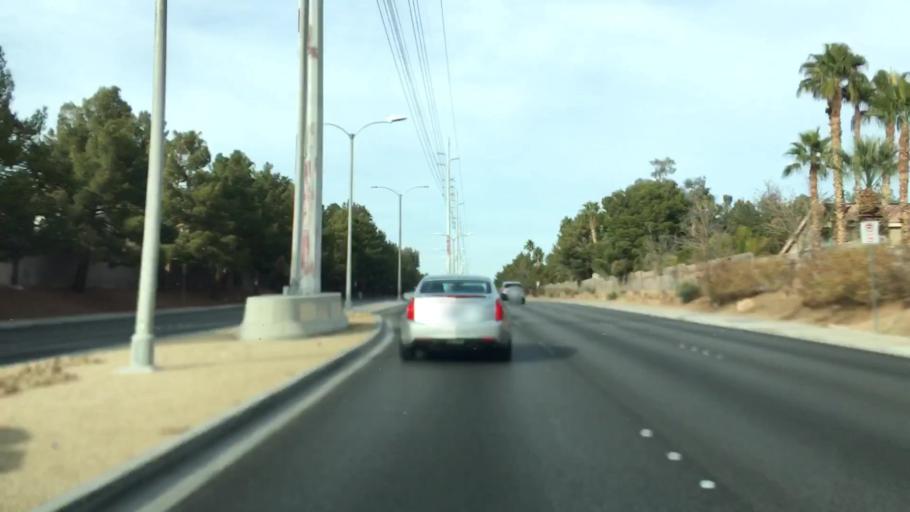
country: US
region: Nevada
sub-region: Clark County
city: Whitney
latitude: 36.0449
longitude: -115.0823
